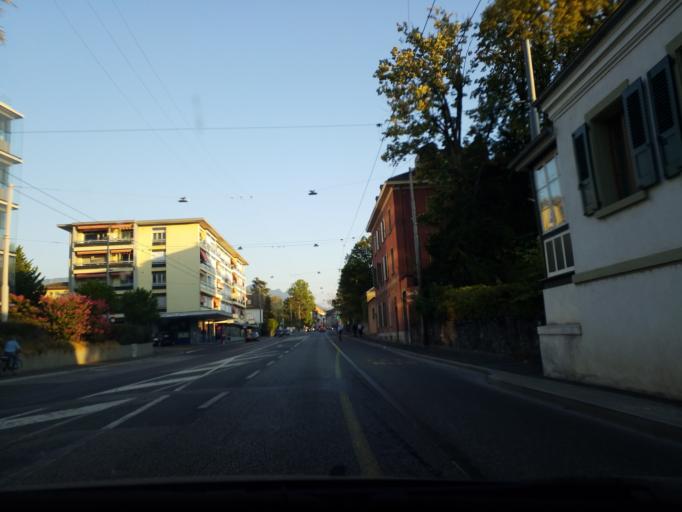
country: CH
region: Vaud
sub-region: Riviera-Pays-d'Enhaut District
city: La Tour-de-Peilz
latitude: 46.4562
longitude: 6.8540
